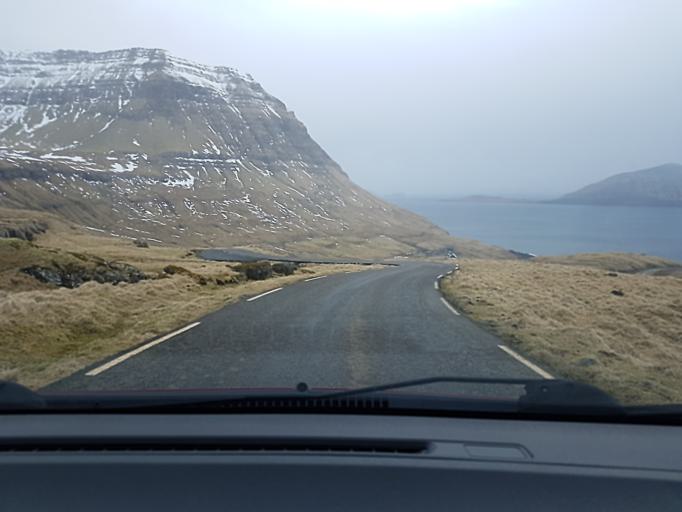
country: FO
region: Streymoy
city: Kollafjordhur
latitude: 62.0484
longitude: -6.9230
